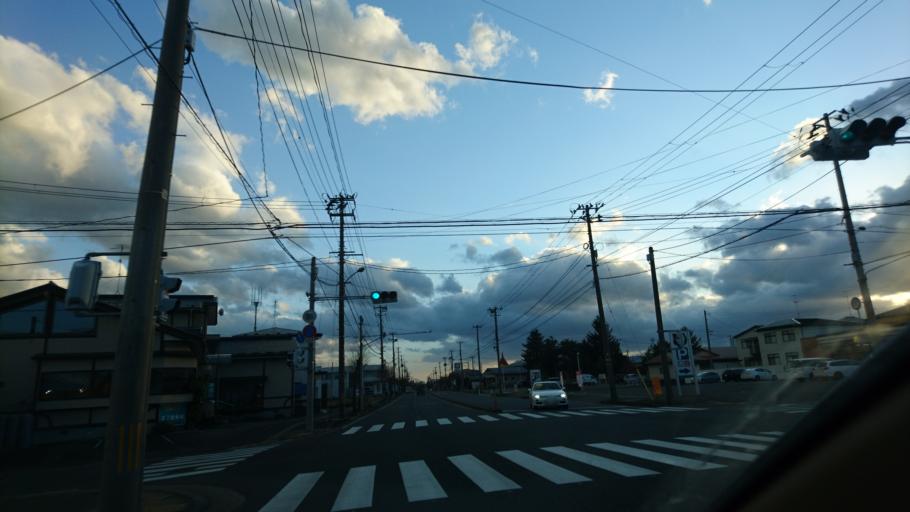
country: JP
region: Iwate
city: Mizusawa
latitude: 39.1524
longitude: 141.1334
